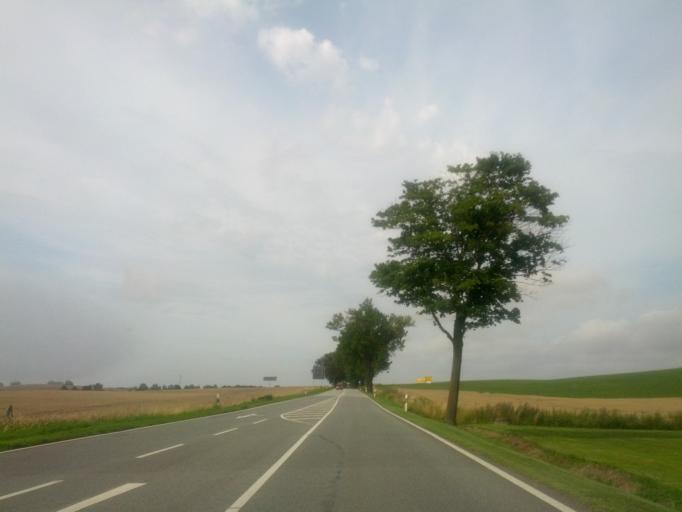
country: DE
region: Mecklenburg-Vorpommern
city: Sellin
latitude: 53.9434
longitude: 11.6126
